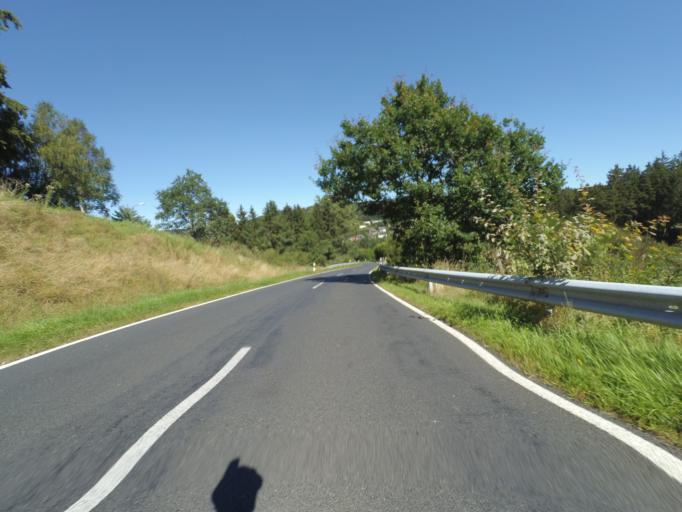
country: DE
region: Rheinland-Pfalz
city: Junkerath
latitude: 50.3439
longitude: 6.5727
